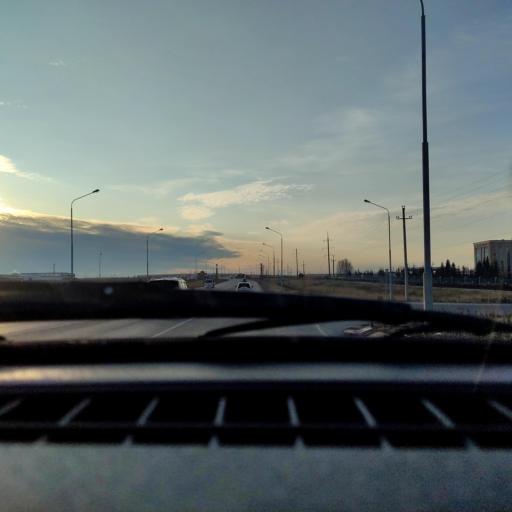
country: RU
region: Bashkortostan
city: Iglino
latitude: 54.7705
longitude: 56.2593
